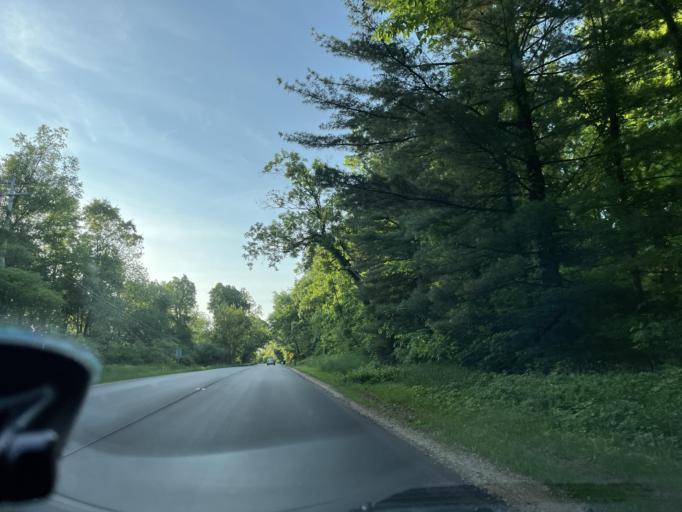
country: US
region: Michigan
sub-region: Barry County
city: Middleville
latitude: 42.7122
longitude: -85.4462
